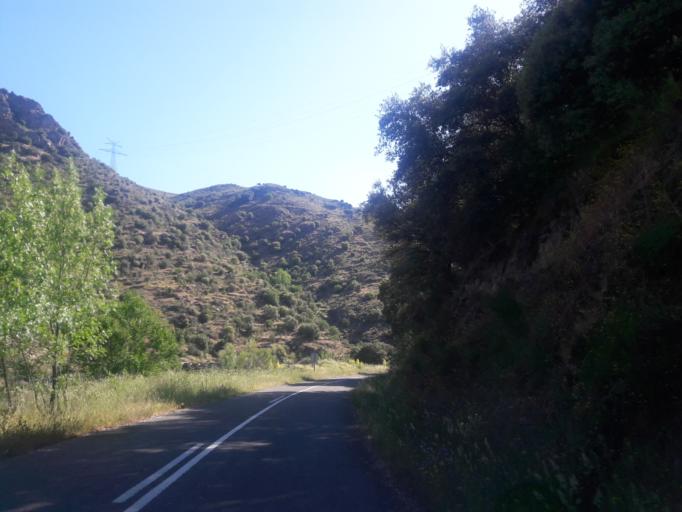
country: ES
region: Castille and Leon
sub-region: Provincia de Salamanca
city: Saucelle
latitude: 41.0287
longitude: -6.7322
